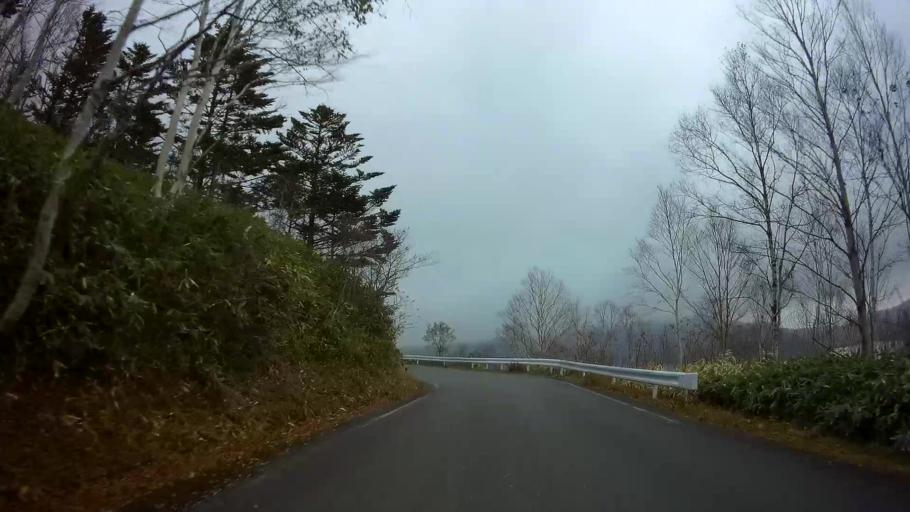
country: JP
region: Gunma
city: Nakanojomachi
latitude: 36.7105
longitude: 138.6523
